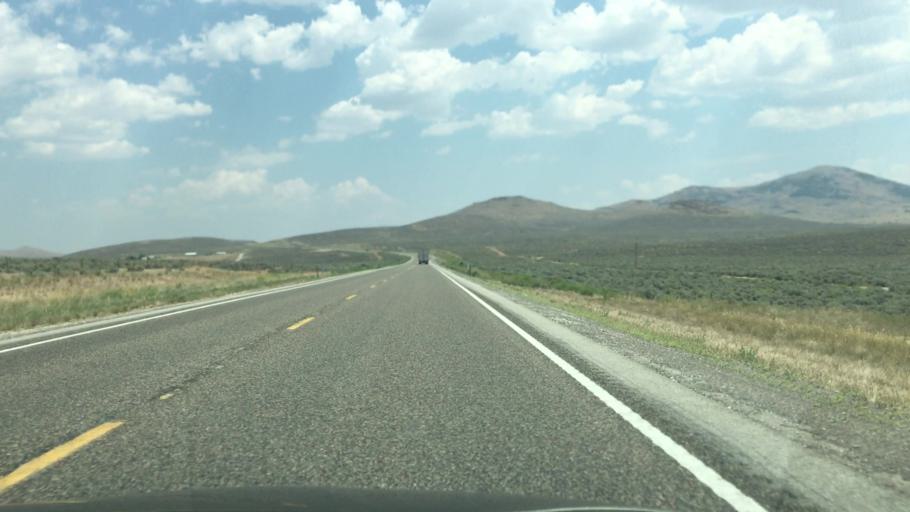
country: US
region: Nevada
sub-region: Elko County
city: Wells
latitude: 41.1673
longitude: -114.8864
